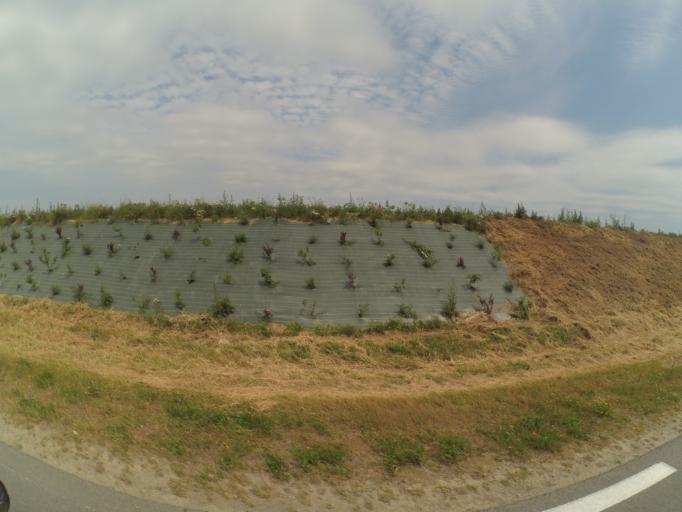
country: FR
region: Pays de la Loire
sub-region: Departement de la Vendee
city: Saint-Paul-en-Pareds
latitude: 46.8446
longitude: -0.9994
